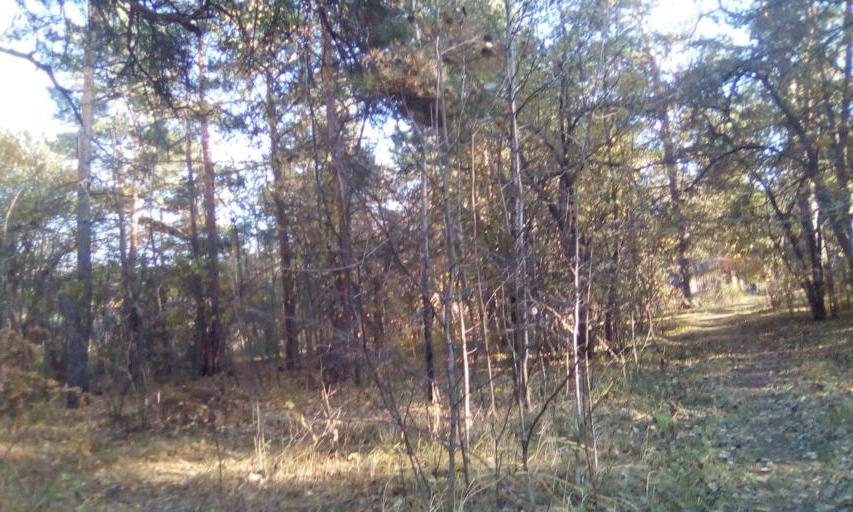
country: RU
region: Chelyabinsk
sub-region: Gorod Chelyabinsk
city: Chelyabinsk
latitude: 55.1592
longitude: 61.3579
